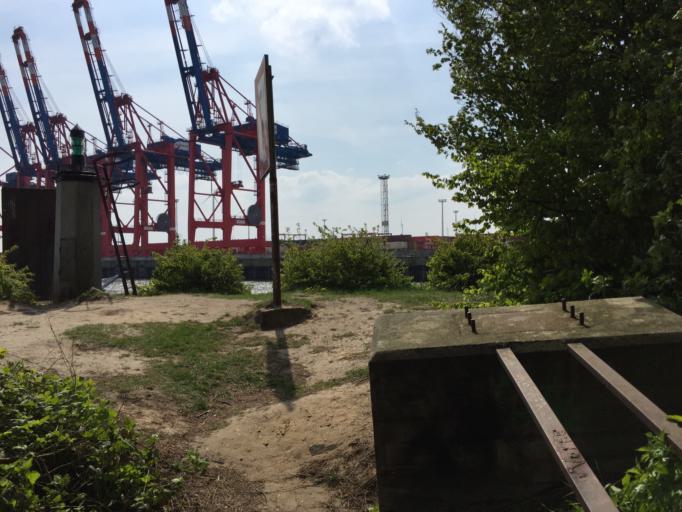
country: DE
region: Hamburg
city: Altona
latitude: 53.5366
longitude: 9.9012
